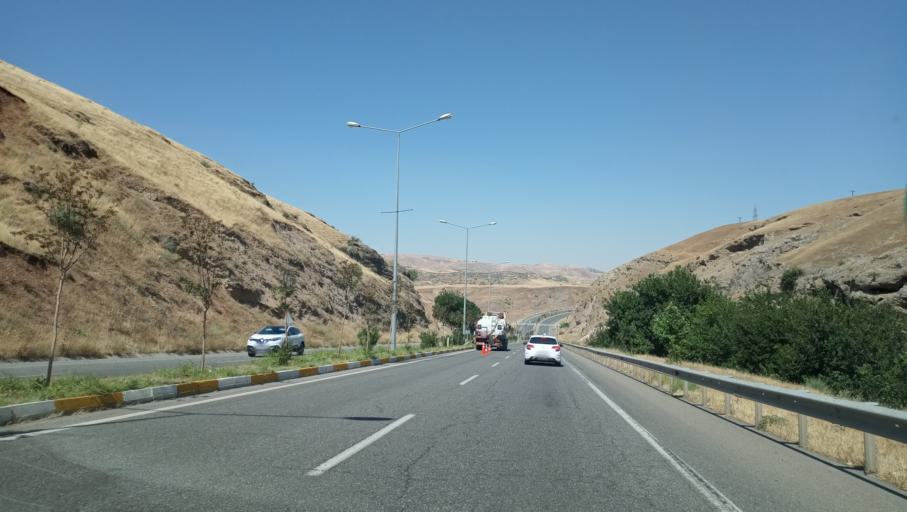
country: TR
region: Siirt
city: Civankan
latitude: 37.9490
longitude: 41.8695
